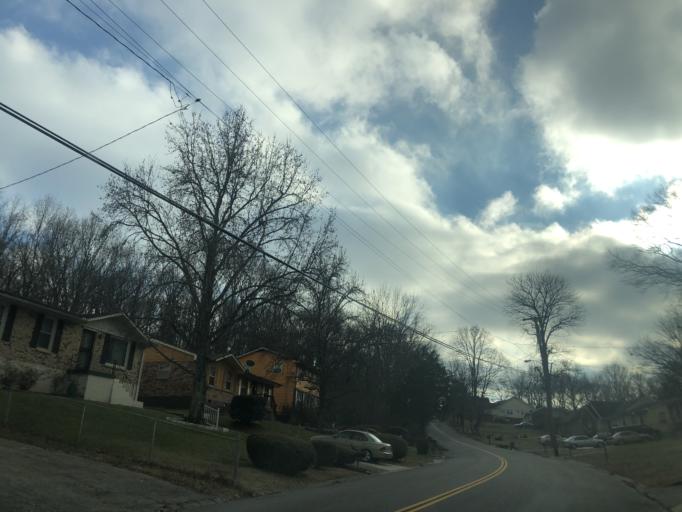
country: US
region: Tennessee
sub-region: Davidson County
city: Nashville
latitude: 36.2171
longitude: -86.7944
